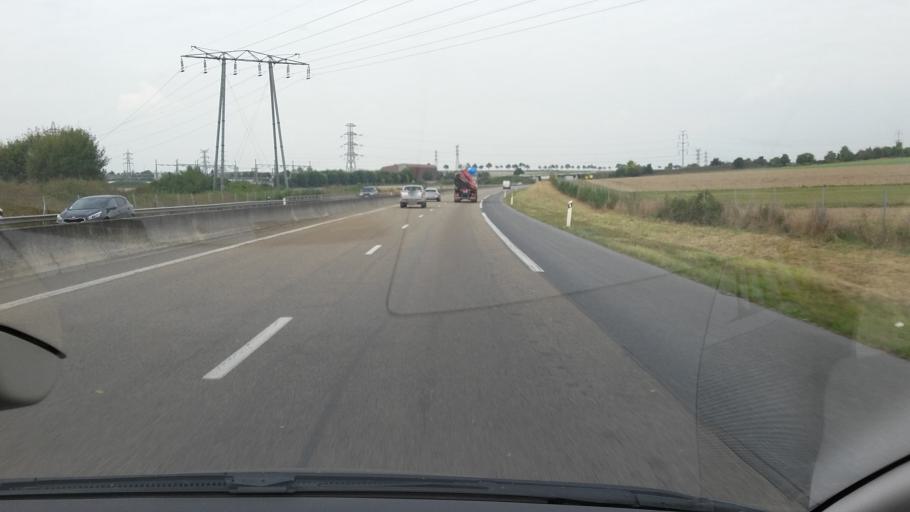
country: FR
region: Champagne-Ardenne
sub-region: Departement de la Marne
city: Cernay-les-Reims
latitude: 49.2670
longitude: 4.0865
